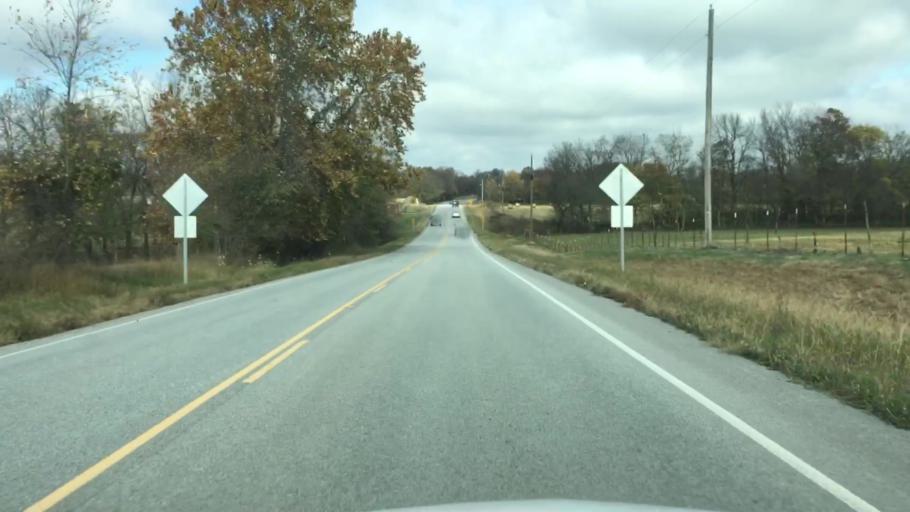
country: US
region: Arkansas
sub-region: Benton County
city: Centerton
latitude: 36.2892
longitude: -94.3455
